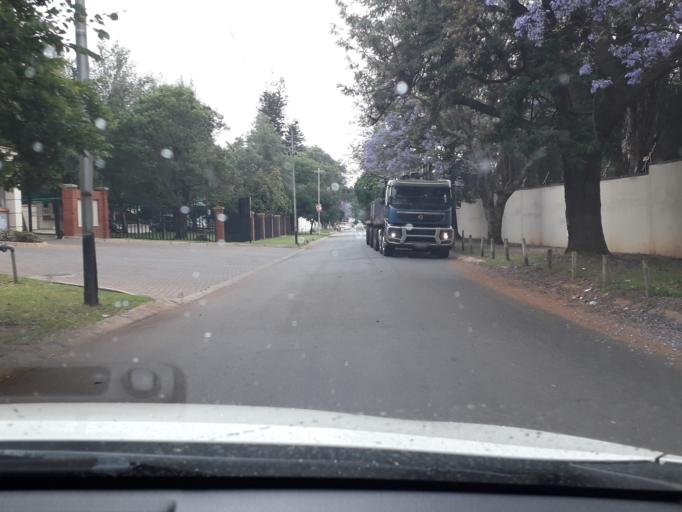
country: ZA
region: Gauteng
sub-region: City of Johannesburg Metropolitan Municipality
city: Johannesburg
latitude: -26.1175
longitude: 28.0507
